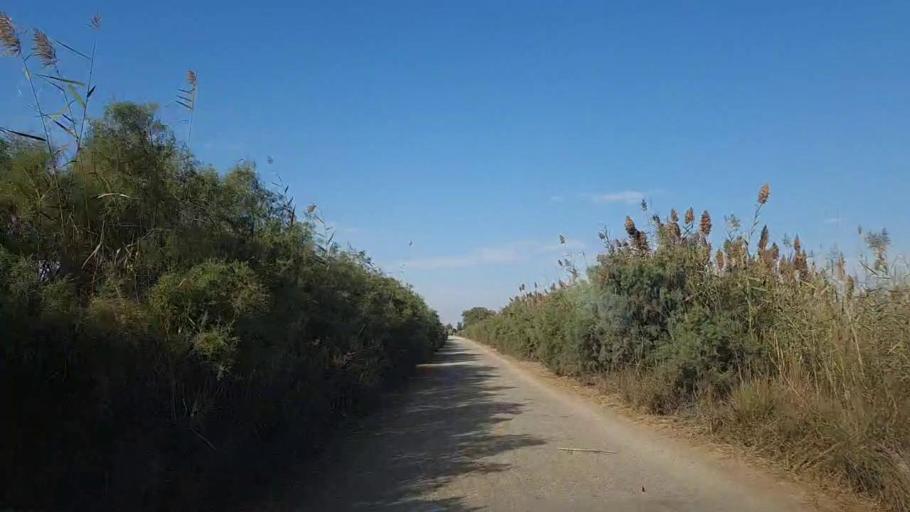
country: PK
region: Sindh
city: Khadro
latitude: 26.2976
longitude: 68.8202
